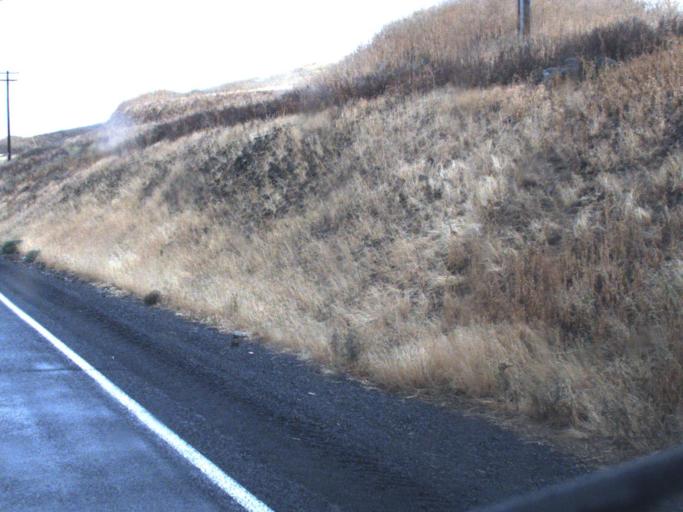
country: US
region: Washington
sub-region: Whitman County
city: Colfax
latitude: 47.0622
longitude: -117.5241
